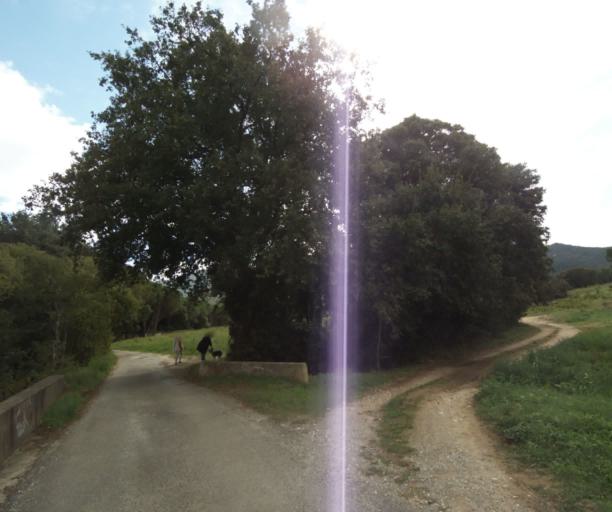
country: FR
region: Languedoc-Roussillon
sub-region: Departement des Pyrenees-Orientales
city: Argelers
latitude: 42.5376
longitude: 3.0232
